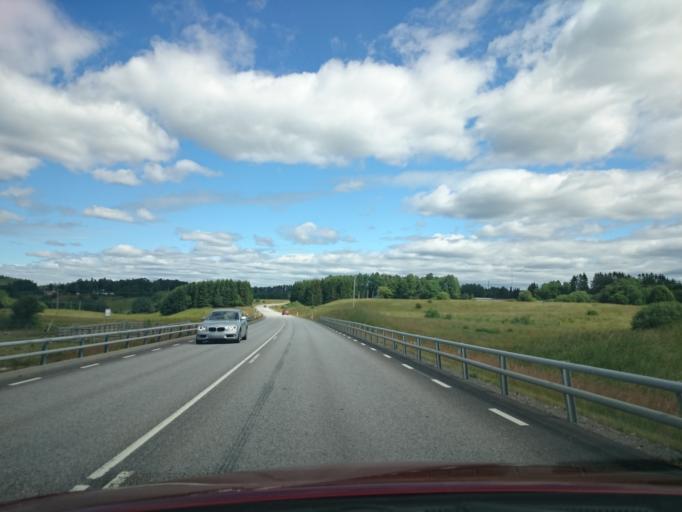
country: SE
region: Vaestra Goetaland
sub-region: Lerums Kommun
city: Stenkullen
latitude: 57.7914
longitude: 12.3015
